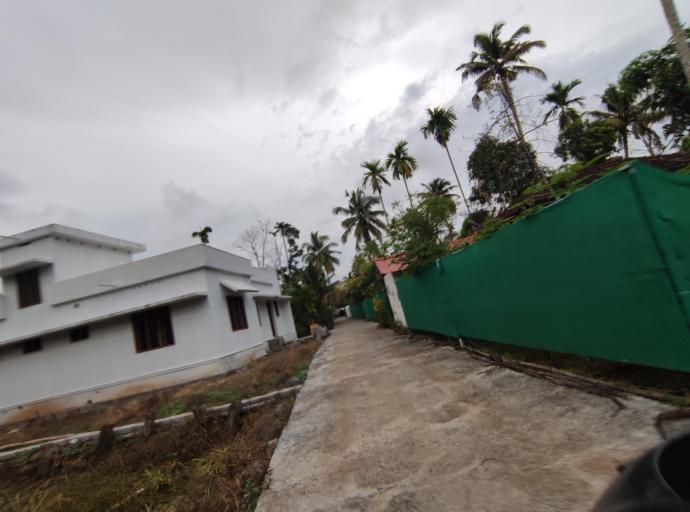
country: IN
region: Kerala
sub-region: Alappuzha
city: Shertallai
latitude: 9.6306
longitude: 76.4256
